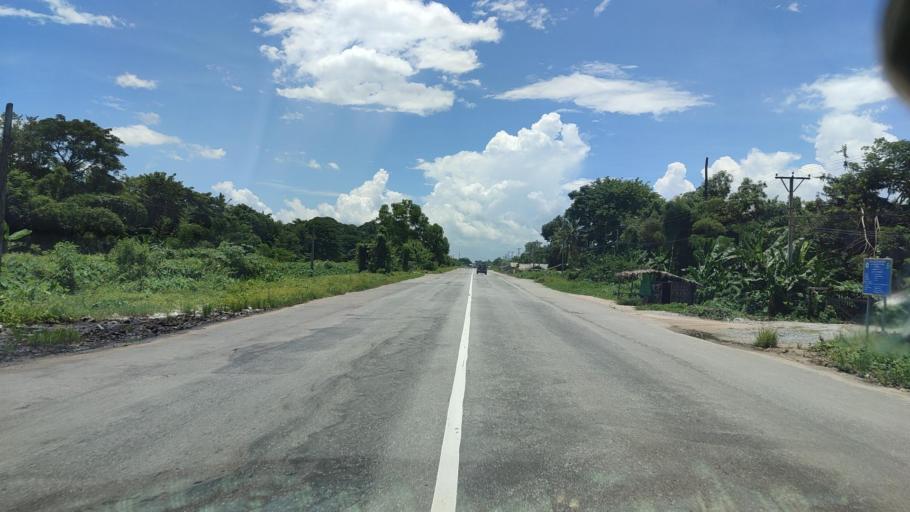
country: MM
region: Bago
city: Taungoo
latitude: 18.7210
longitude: 96.4077
